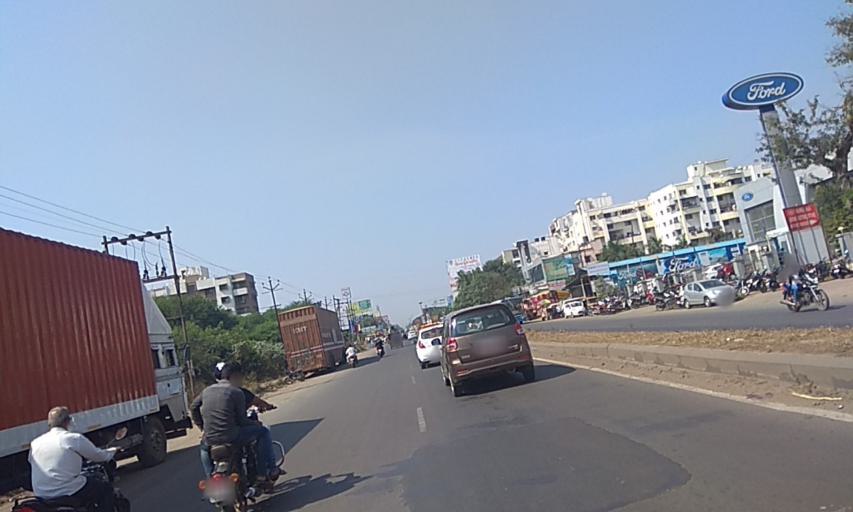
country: IN
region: Maharashtra
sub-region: Pune Division
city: Lohogaon
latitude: 18.4973
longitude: 73.9640
